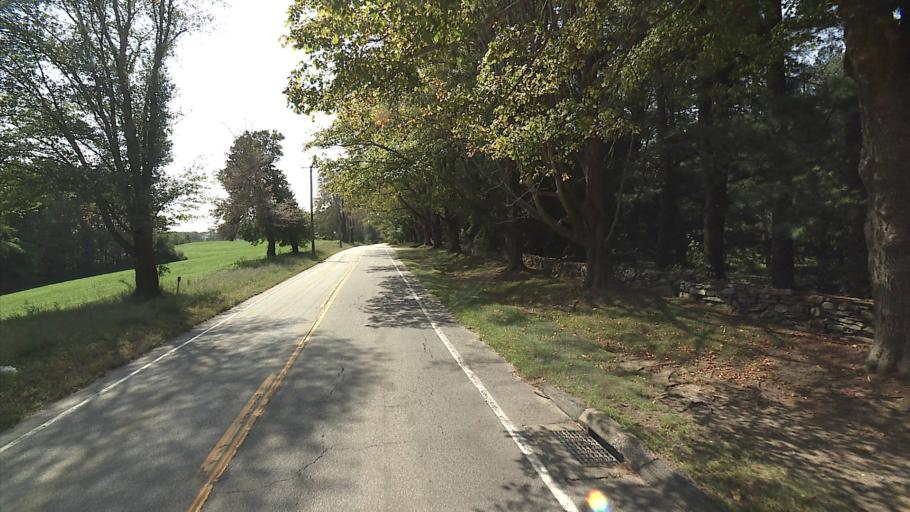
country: US
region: Connecticut
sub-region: Windham County
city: South Woodstock
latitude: 41.9161
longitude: -71.9560
